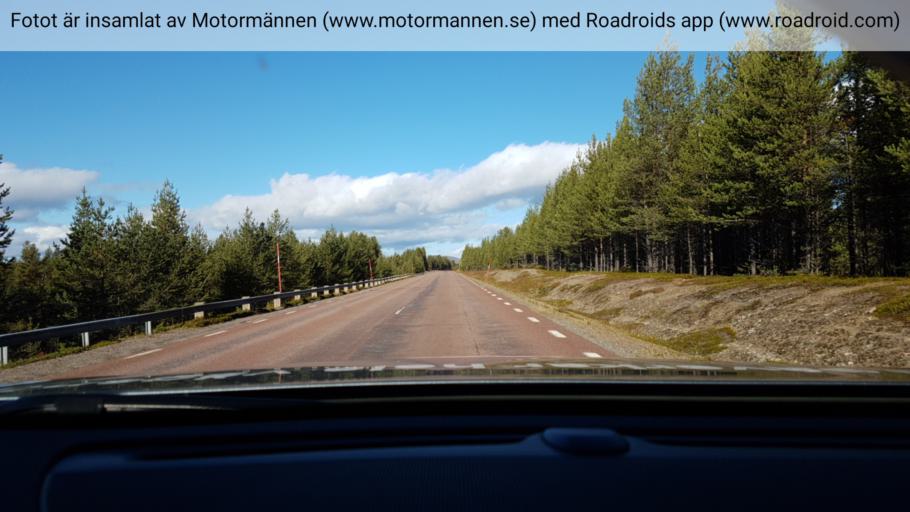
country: SE
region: Norrbotten
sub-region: Arjeplogs Kommun
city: Arjeplog
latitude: 66.0230
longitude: 18.0700
